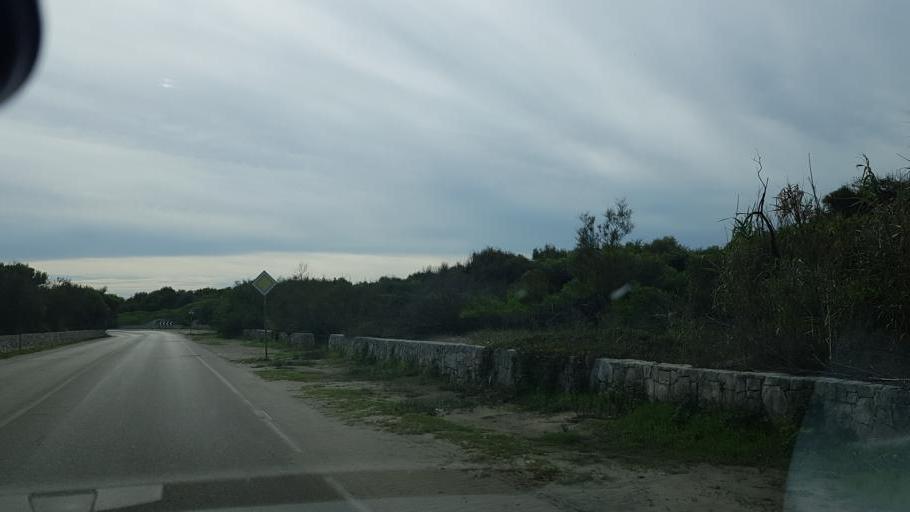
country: IT
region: Apulia
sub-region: Provincia di Lecce
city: Borgagne
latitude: 40.2980
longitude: 18.4091
